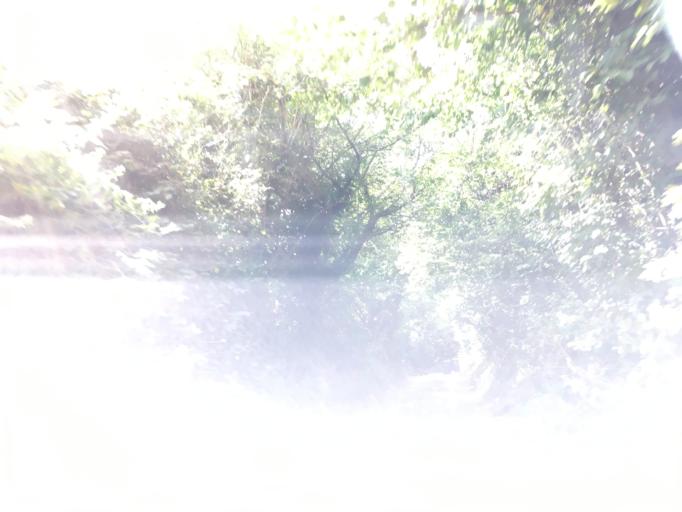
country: GB
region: England
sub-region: Kent
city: West Malling
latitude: 51.2991
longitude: 0.3948
